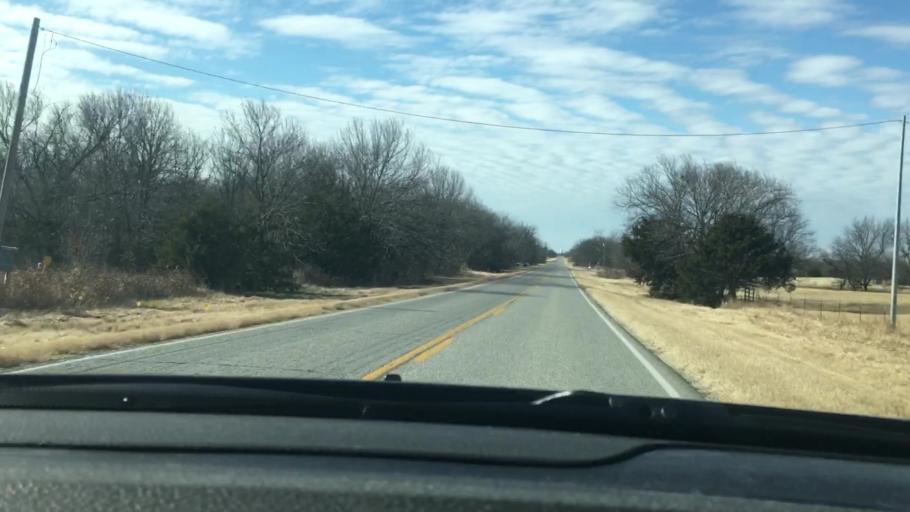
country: US
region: Oklahoma
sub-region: Garvin County
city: Wynnewood
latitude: 34.6516
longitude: -97.1232
